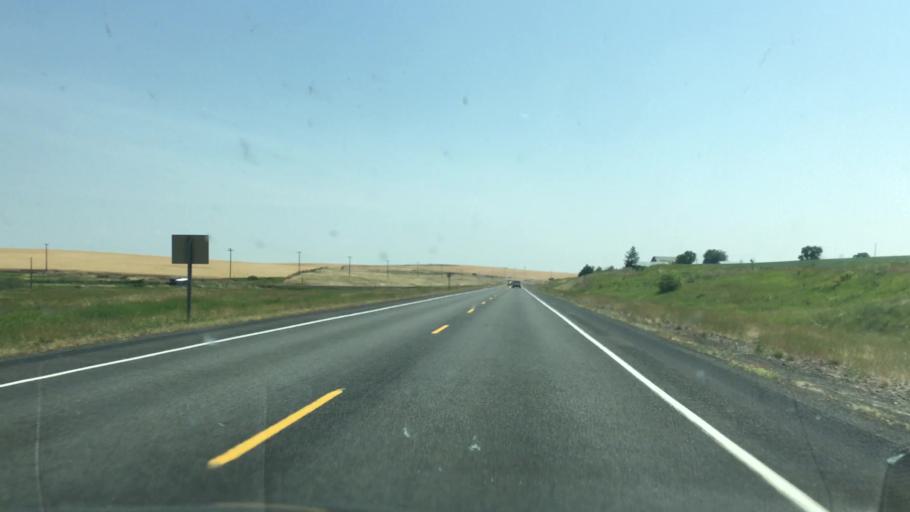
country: US
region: Idaho
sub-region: Lewis County
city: Nezperce
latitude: 46.2303
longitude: -116.4575
